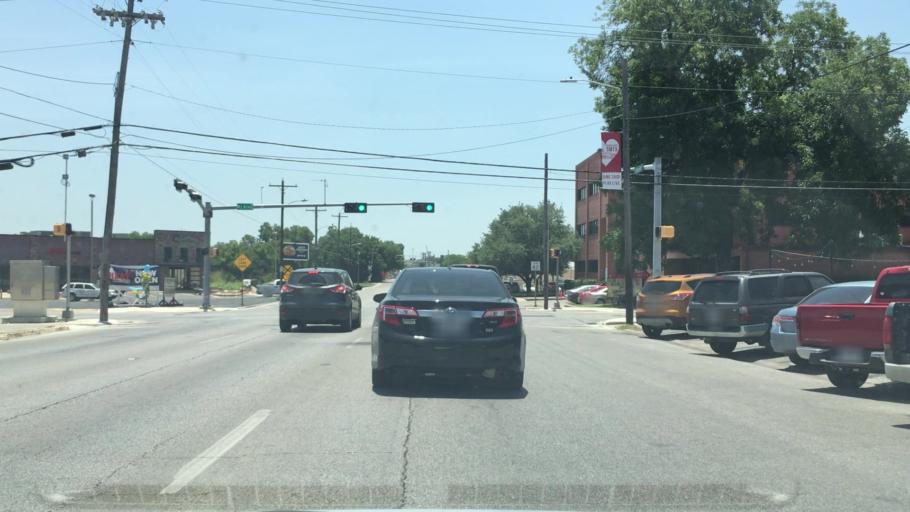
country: US
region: Texas
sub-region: Hays County
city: San Marcos
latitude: 29.8805
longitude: -97.9411
